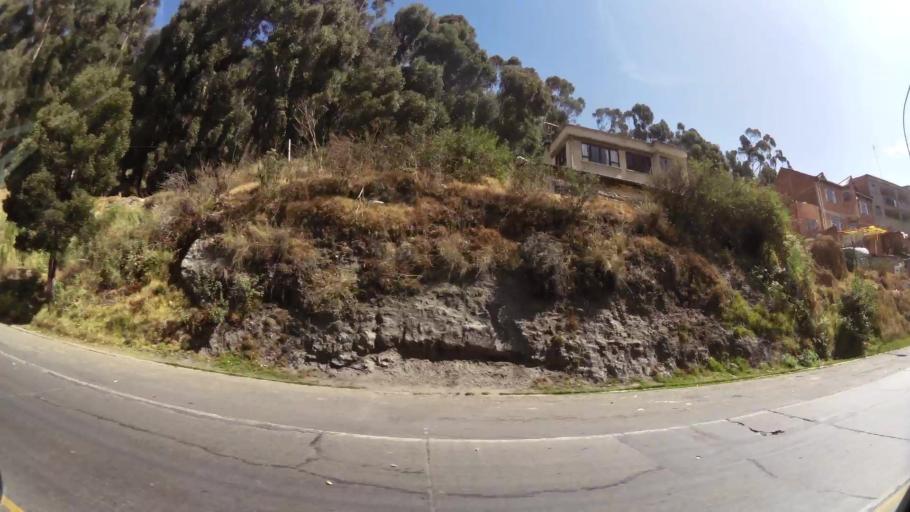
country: BO
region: La Paz
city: La Paz
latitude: -16.4753
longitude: -68.1532
